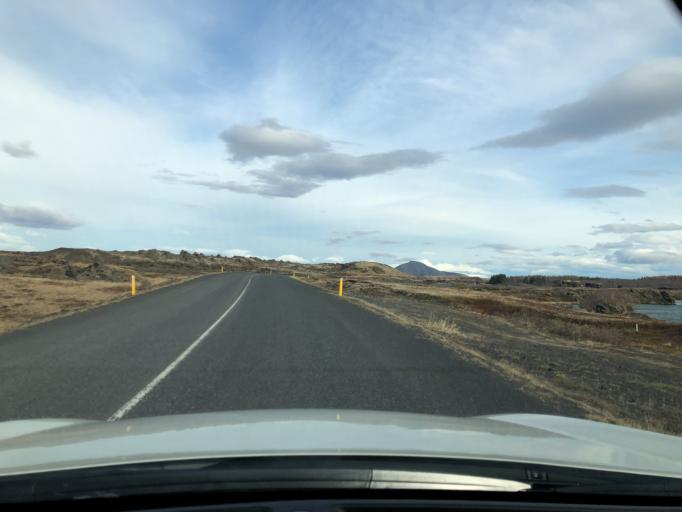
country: IS
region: Northeast
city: Laugar
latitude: 65.5703
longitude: -16.9451
